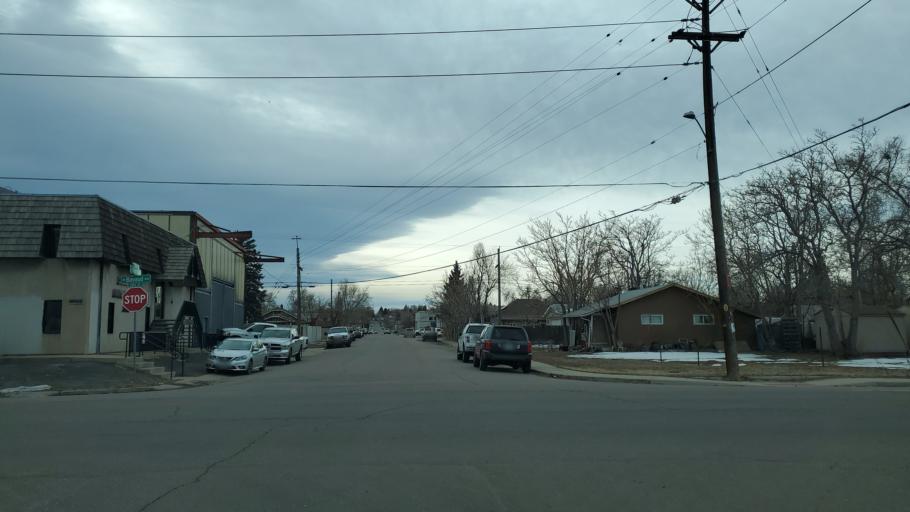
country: US
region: Colorado
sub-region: Denver County
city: Denver
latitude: 39.7150
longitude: -105.0087
